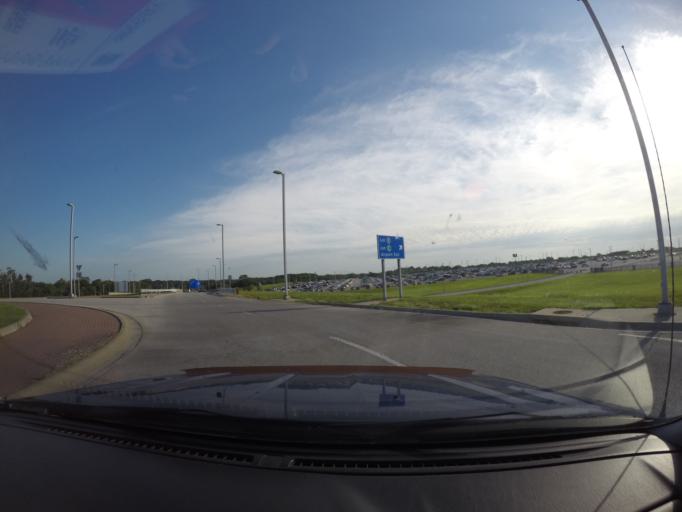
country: US
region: Missouri
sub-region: Platte County
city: Weatherby Lake
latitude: 39.3147
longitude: -94.6997
